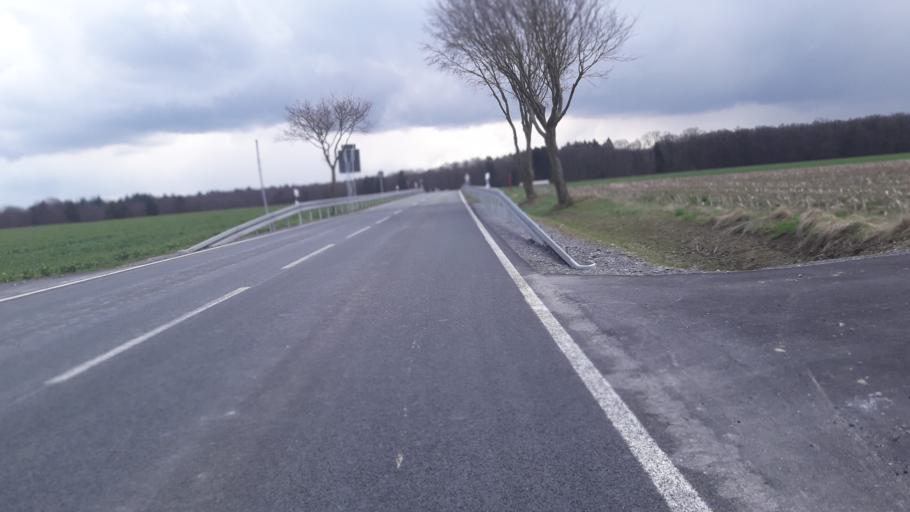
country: DE
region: North Rhine-Westphalia
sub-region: Regierungsbezirk Detmold
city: Wunnenberg
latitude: 51.4978
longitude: 8.6772
